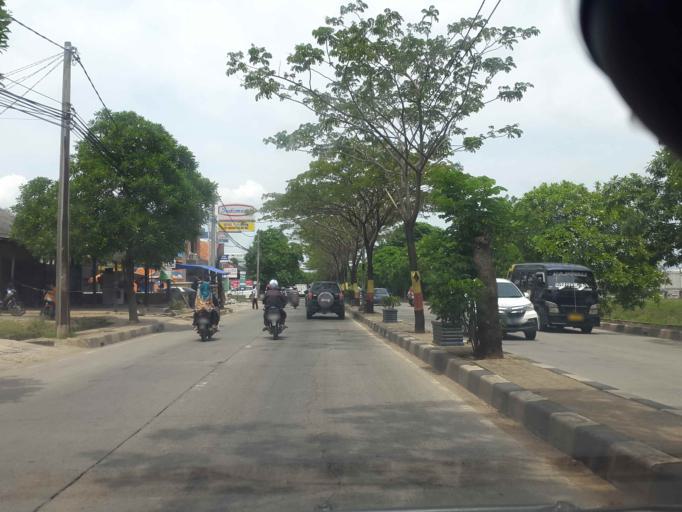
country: ID
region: Banten
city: Tangerang
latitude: -6.1428
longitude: 106.6327
